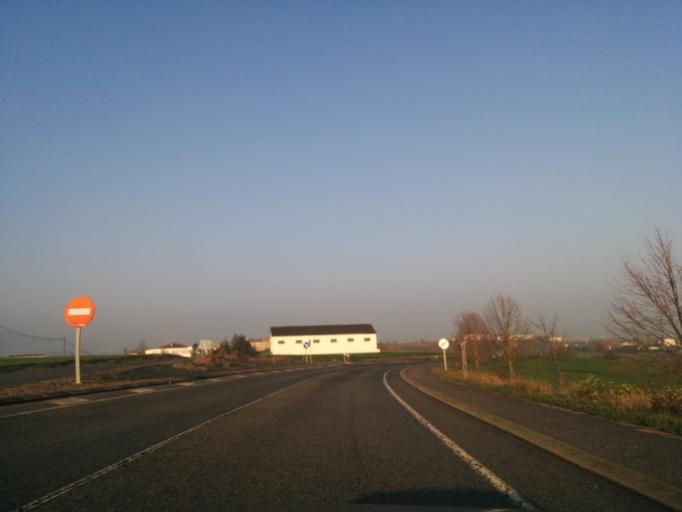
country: ES
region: Navarre
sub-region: Provincia de Navarra
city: Elorz
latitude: 42.7688
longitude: -1.6002
